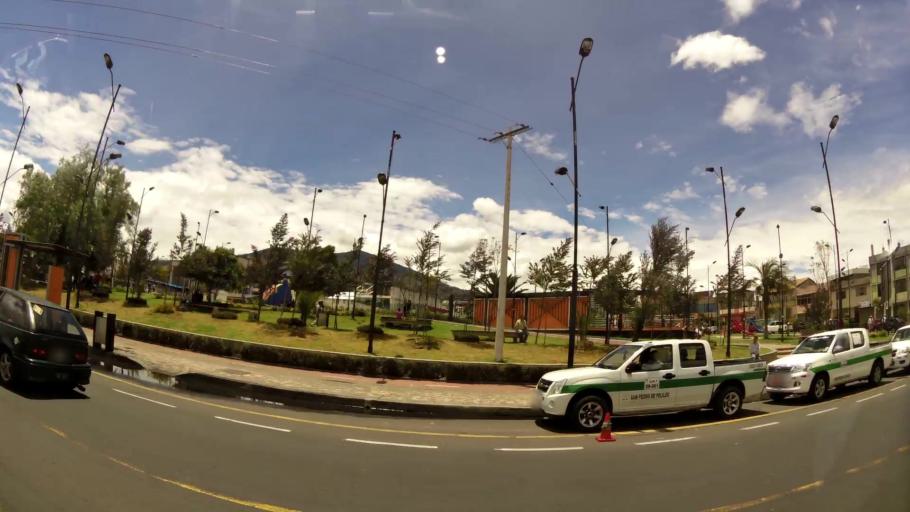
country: EC
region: Tungurahua
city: Pelileo
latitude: -1.3272
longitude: -78.5416
